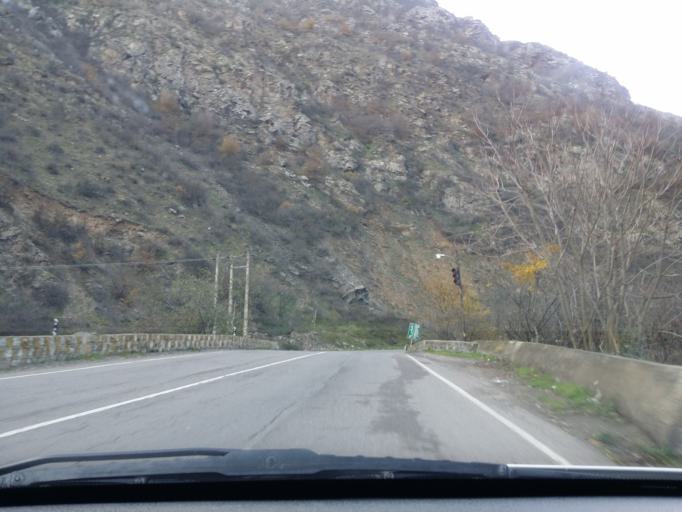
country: IR
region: Mazandaran
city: Chalus
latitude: 36.3054
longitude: 51.2475
